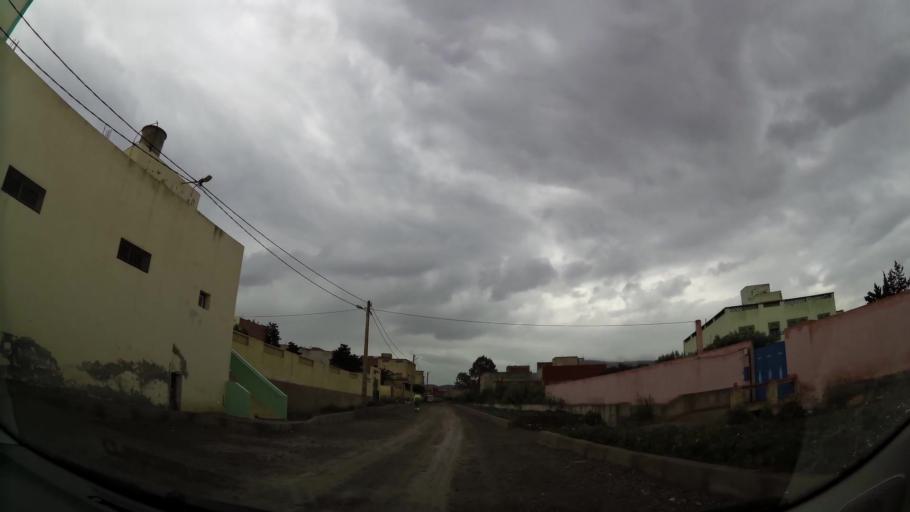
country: MA
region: Oriental
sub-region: Nador
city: Nador
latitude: 35.1486
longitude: -2.9830
